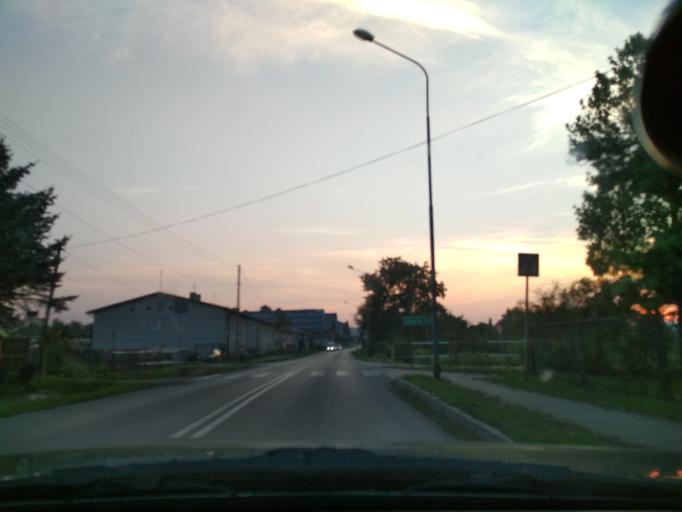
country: PL
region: Silesian Voivodeship
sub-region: Powiat zawiercianski
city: Pilica
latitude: 50.4684
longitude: 19.6831
